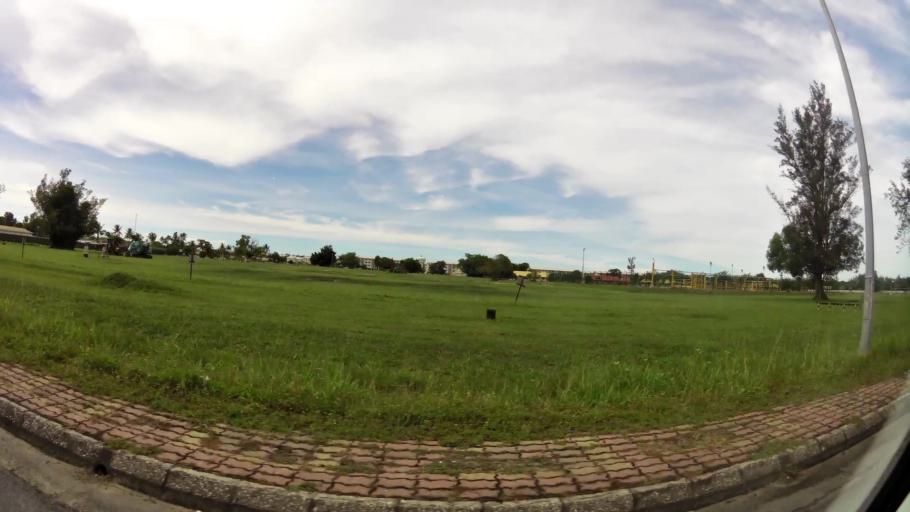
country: BN
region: Belait
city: Seria
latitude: 4.6093
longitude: 114.3106
